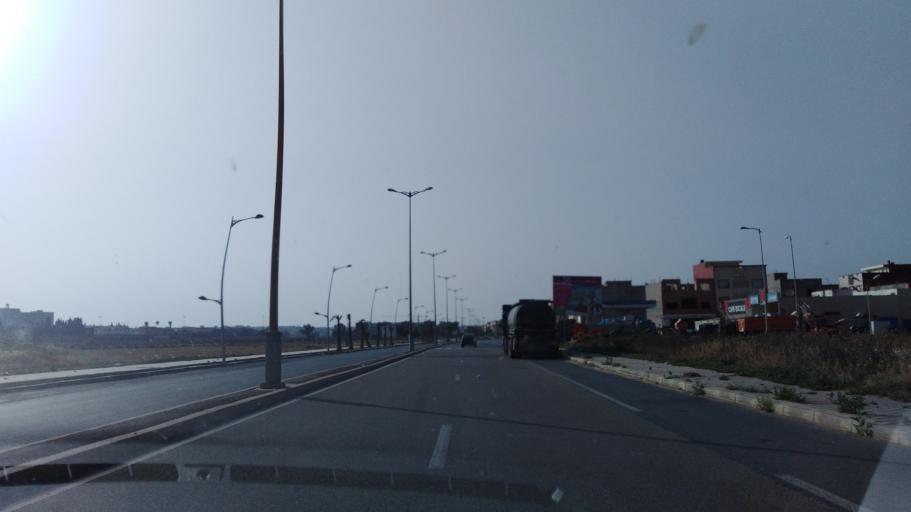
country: MA
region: Chaouia-Ouardigha
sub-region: Settat Province
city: Settat
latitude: 32.9813
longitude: -7.6072
